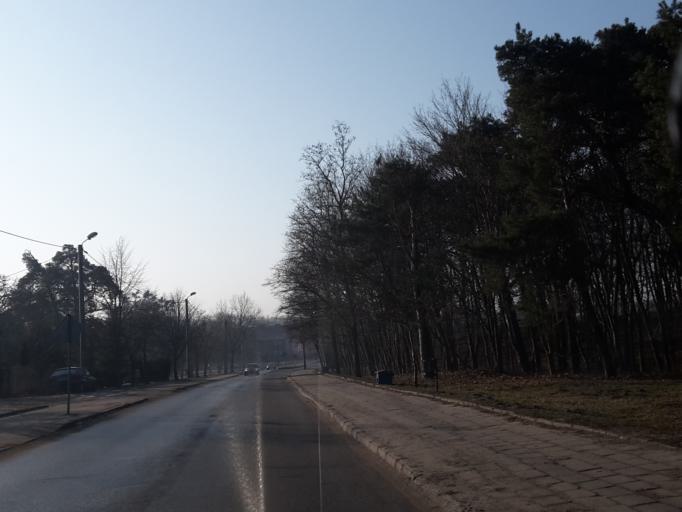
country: PL
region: Kujawsko-Pomorskie
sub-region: Powiat brodnicki
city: Brodnica
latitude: 53.2671
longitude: 19.4063
